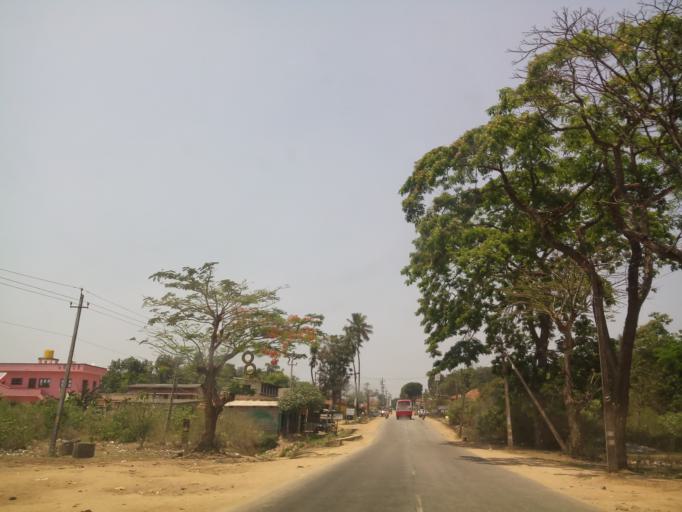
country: IN
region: Karnataka
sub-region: Hassan
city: Sakleshpur
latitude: 12.9449
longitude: 75.8838
